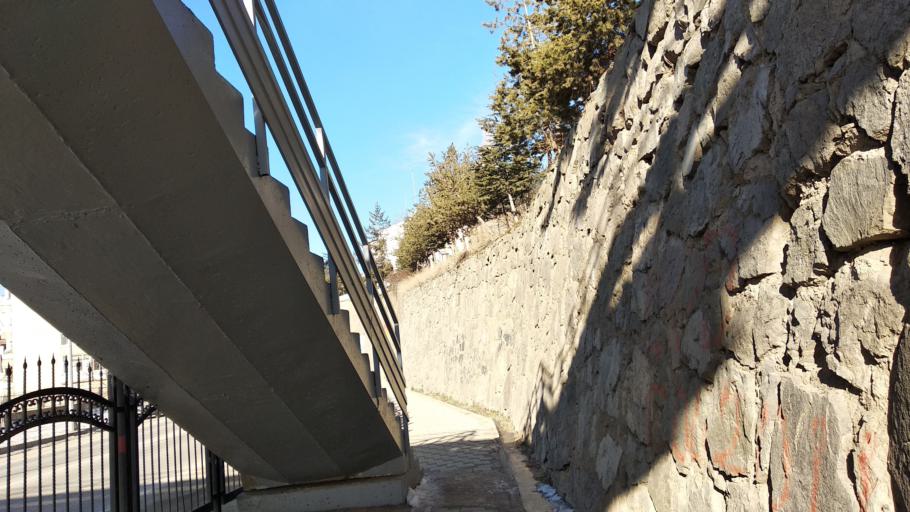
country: TR
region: Gumushane
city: Gumushkhane
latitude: 40.4571
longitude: 39.4892
